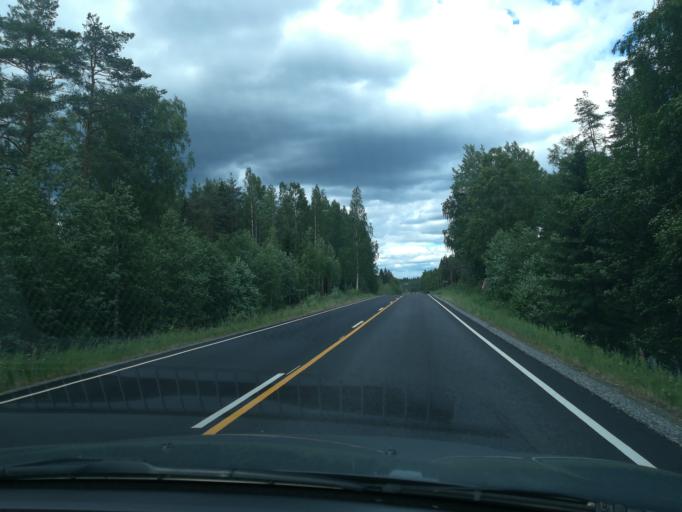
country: FI
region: Southern Savonia
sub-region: Mikkeli
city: Mikkeli
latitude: 61.6541
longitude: 27.0958
